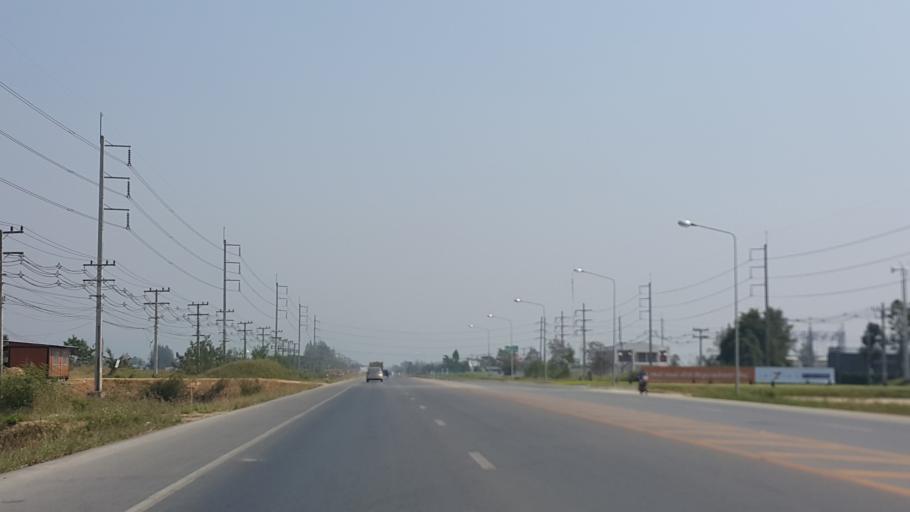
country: TH
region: Chiang Mai
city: San Kamphaeng
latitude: 18.7385
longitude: 99.0841
